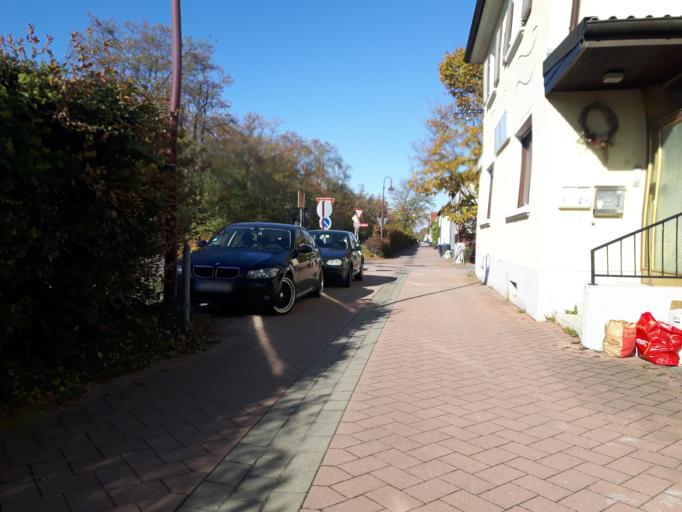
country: DE
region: Rheinland-Pfalz
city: Fussgonheim
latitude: 49.4739
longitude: 8.2832
